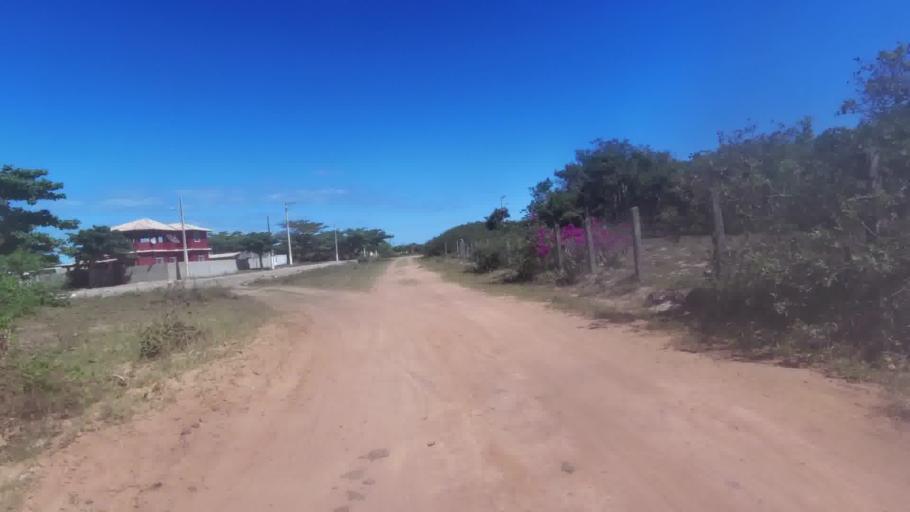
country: BR
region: Espirito Santo
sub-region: Marataizes
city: Marataizes
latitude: -21.1922
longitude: -40.9341
